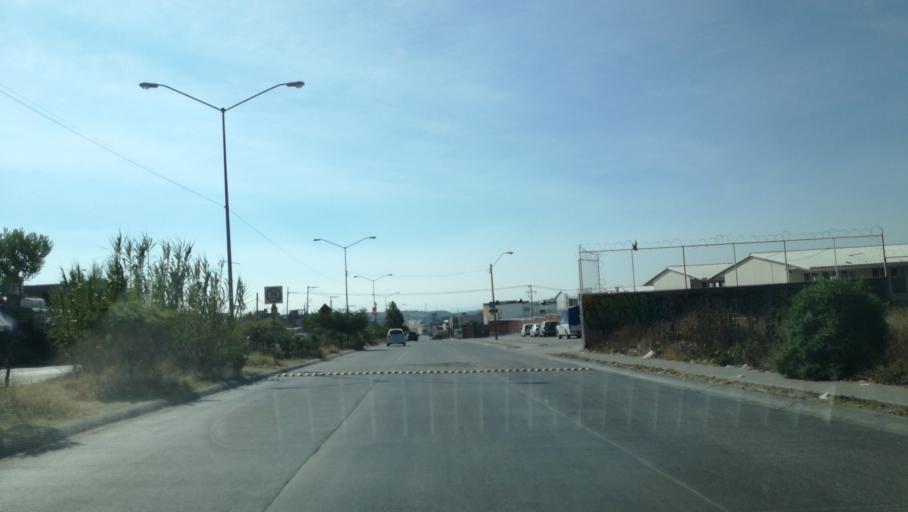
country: MX
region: Guanajuato
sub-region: Leon
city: La Ermita
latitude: 21.1545
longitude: -101.7369
